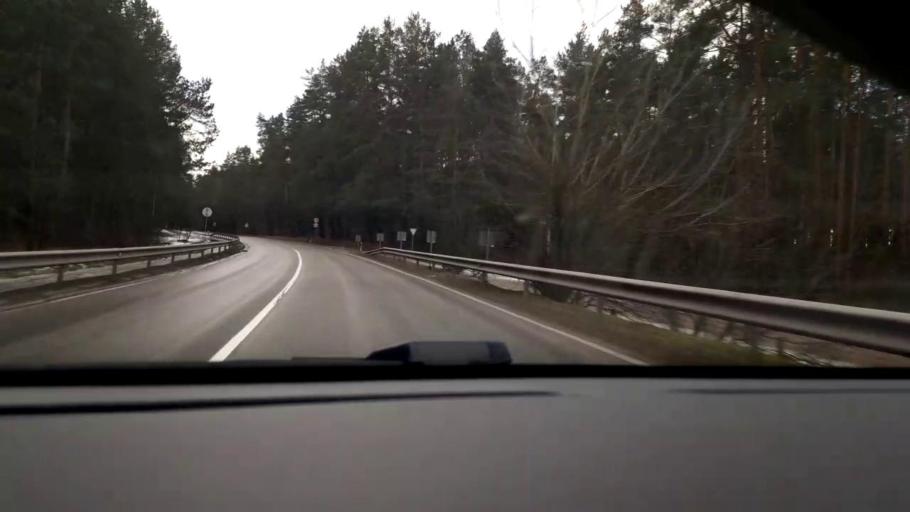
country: LT
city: Nemencine
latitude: 54.7874
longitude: 25.3839
